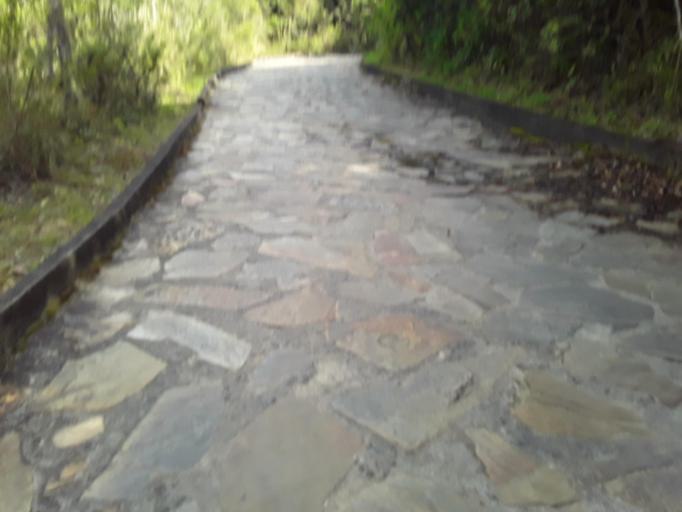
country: BR
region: Minas Gerais
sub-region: Lima Duarte
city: Lima Duarte
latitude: -21.7117
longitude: -43.8962
